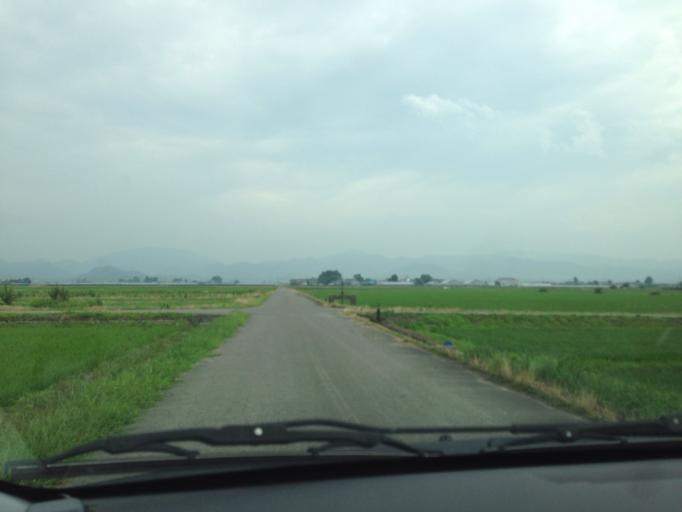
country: JP
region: Fukushima
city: Kitakata
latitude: 37.5006
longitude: 139.8656
